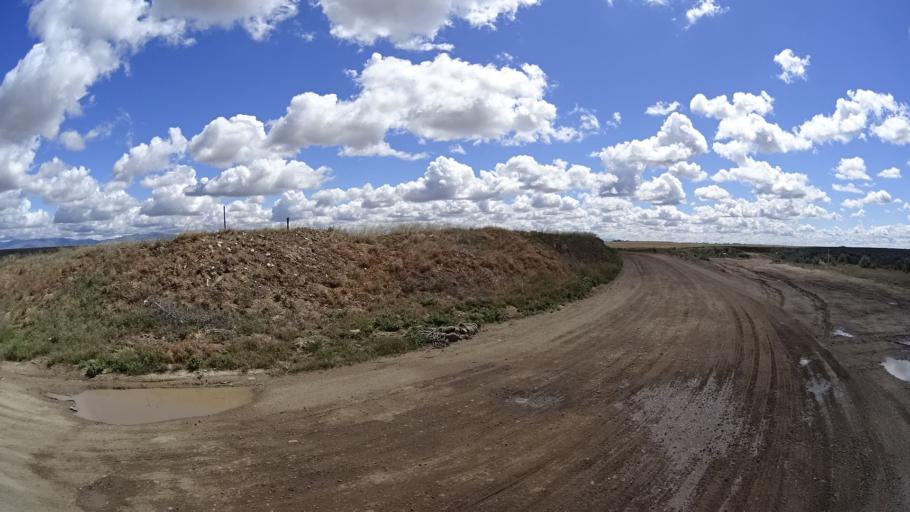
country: US
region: Idaho
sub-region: Ada County
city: Garden City
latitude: 43.4849
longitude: -116.2743
